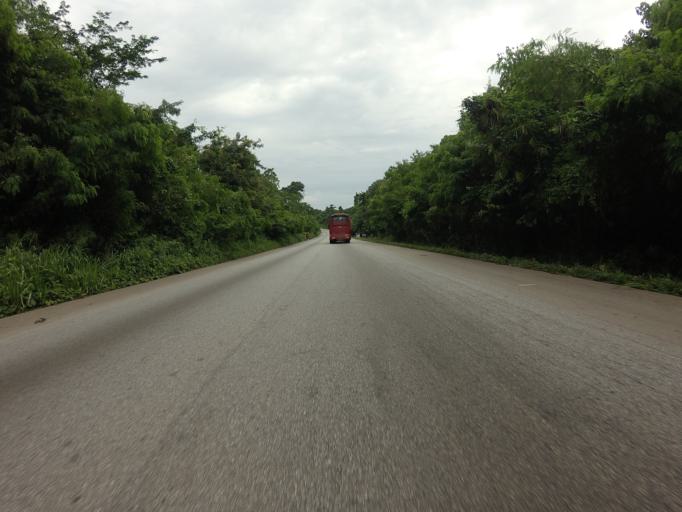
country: GH
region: Eastern
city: Nkawkaw
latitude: 6.6028
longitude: -0.9709
